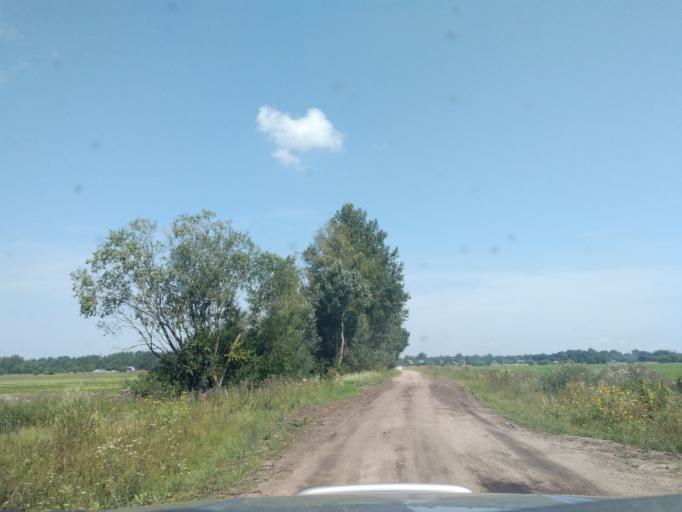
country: BY
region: Minsk
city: Valozhyn
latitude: 54.0025
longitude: 26.5708
